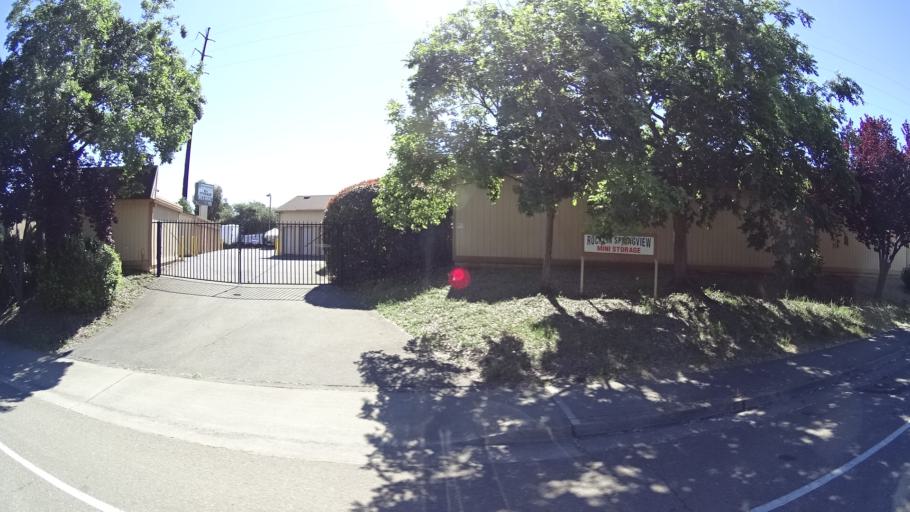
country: US
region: California
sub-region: Placer County
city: Rocklin
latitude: 38.7755
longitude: -121.2501
